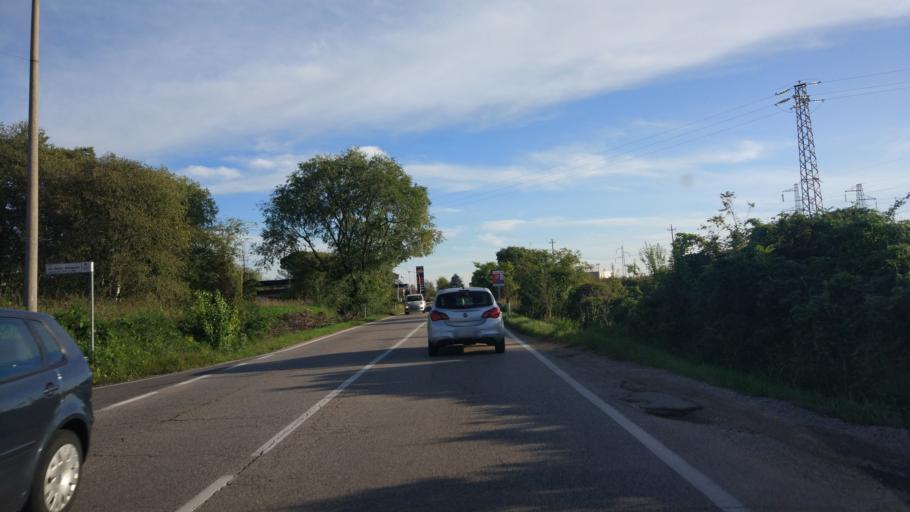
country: IT
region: Veneto
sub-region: Provincia di Verona
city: Sant'Ambrogio di Valpollicella
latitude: 45.5128
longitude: 10.8257
